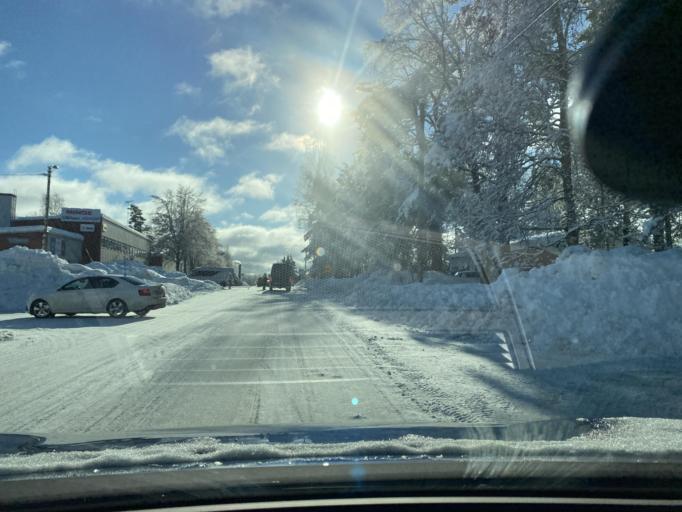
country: FI
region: Southern Savonia
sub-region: Mikkeli
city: Kangasniemi
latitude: 61.9902
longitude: 26.6347
